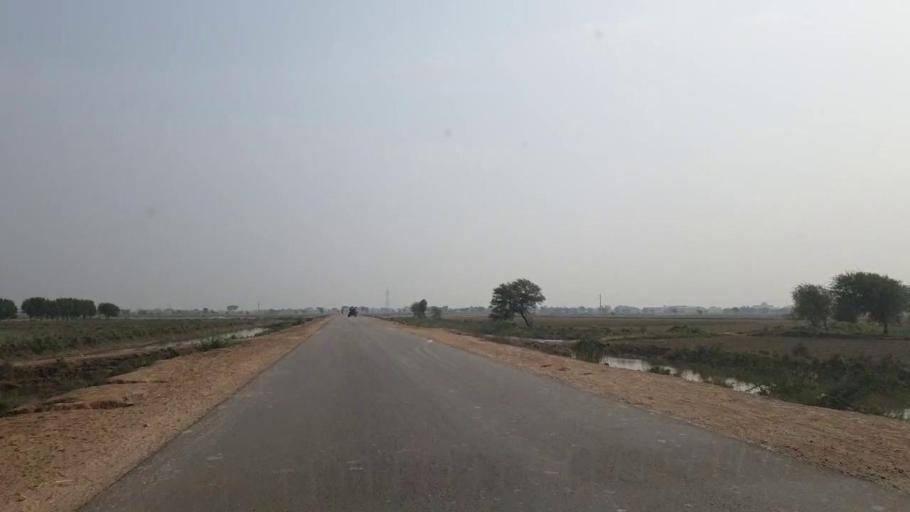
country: PK
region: Sindh
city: Matli
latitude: 25.0599
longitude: 68.6689
